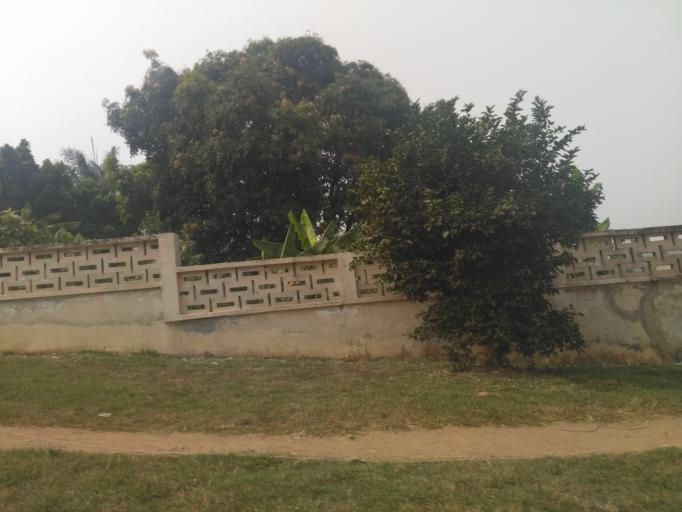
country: GH
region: Ashanti
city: Kumasi
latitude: 6.6961
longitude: -1.6413
